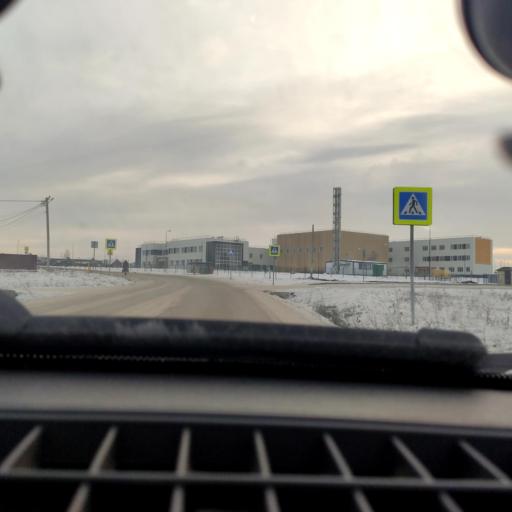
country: RU
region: Bashkortostan
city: Iglino
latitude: 54.8264
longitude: 56.4378
